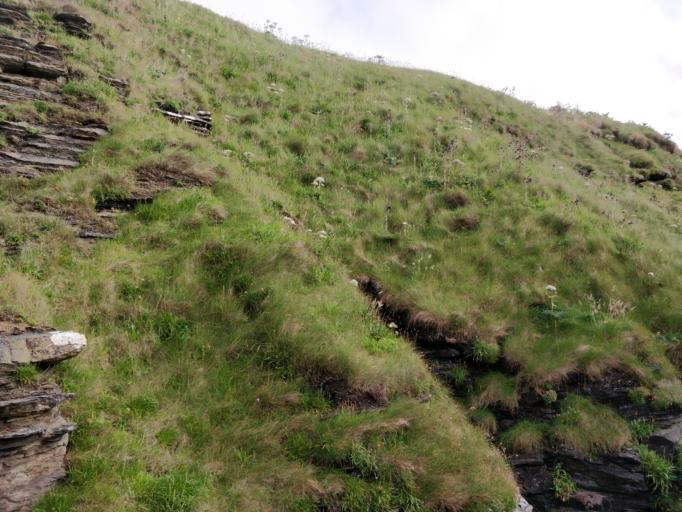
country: GB
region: Scotland
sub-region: Highland
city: Wick
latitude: 58.4779
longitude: -3.0686
